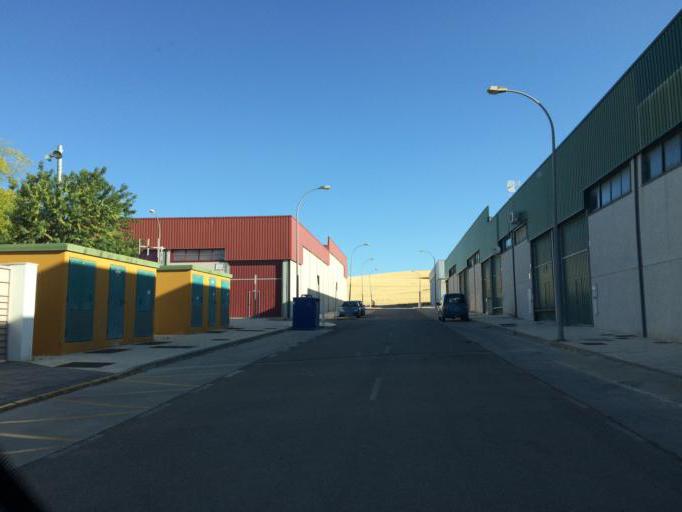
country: ES
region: Andalusia
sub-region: Provincia de Malaga
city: Campillos
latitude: 37.0504
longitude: -4.8750
